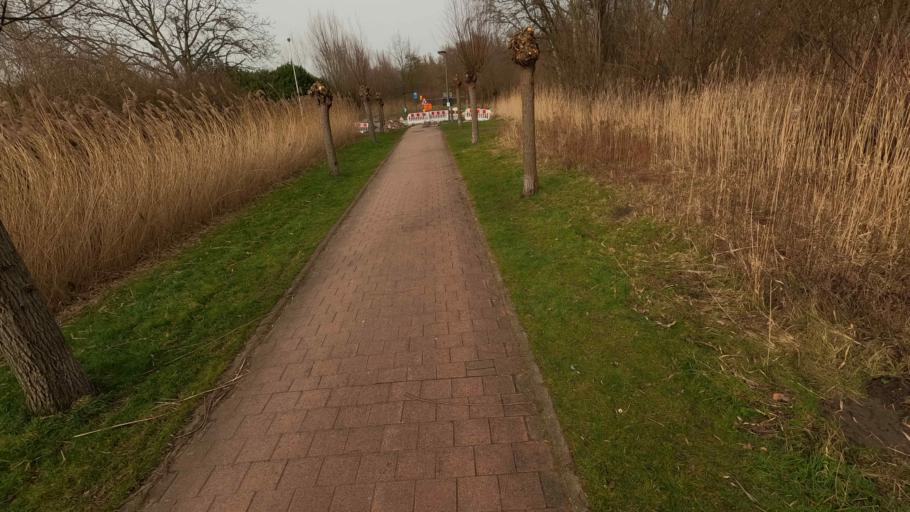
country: BE
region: Flanders
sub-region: Provincie Antwerpen
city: Zwijndrecht
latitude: 51.2228
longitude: 4.3416
